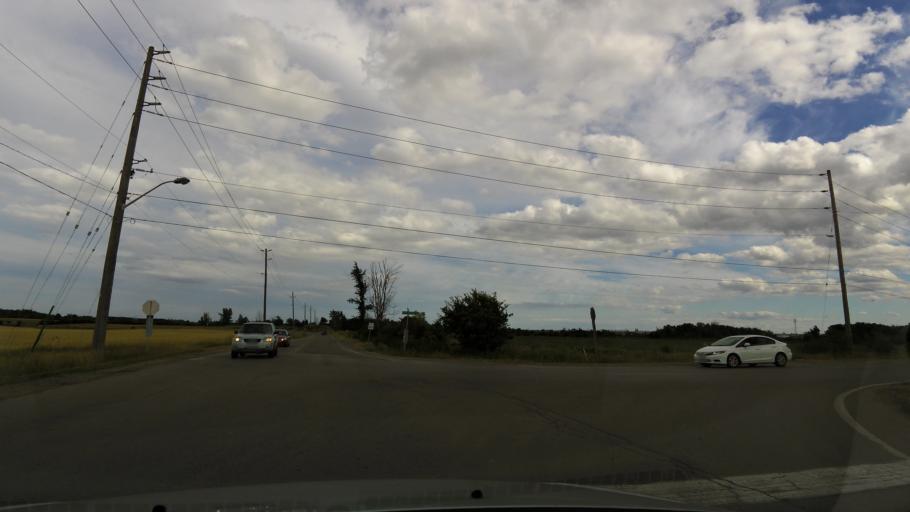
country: CA
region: Ontario
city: Brampton
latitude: 43.6672
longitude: -79.9024
